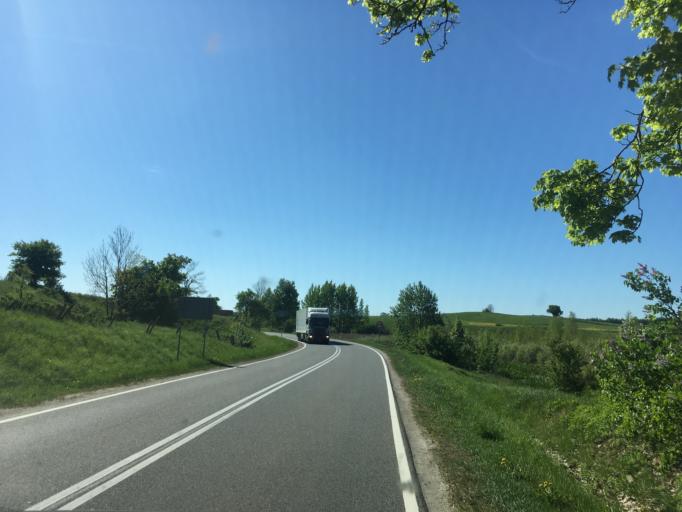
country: PL
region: Warmian-Masurian Voivodeship
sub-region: Powiat mragowski
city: Piecki
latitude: 53.6687
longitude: 21.3364
